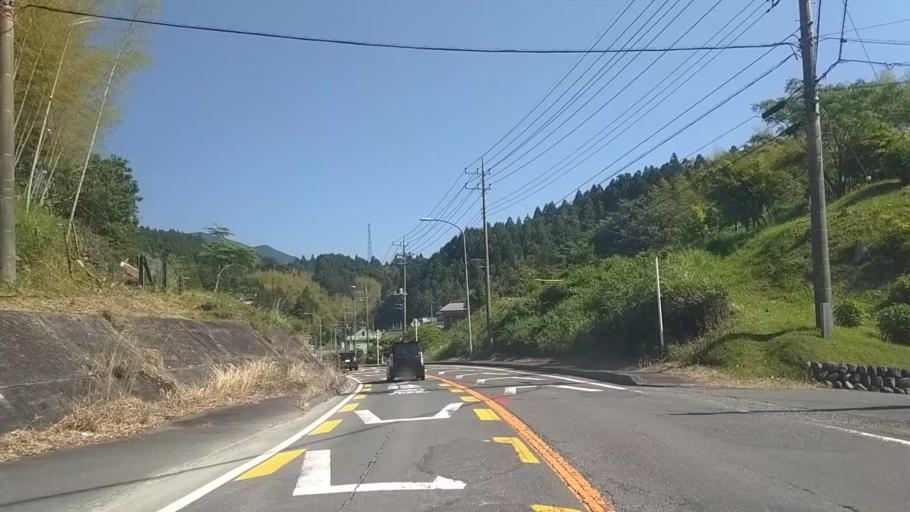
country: JP
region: Shizuoka
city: Fujinomiya
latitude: 35.2764
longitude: 138.4503
